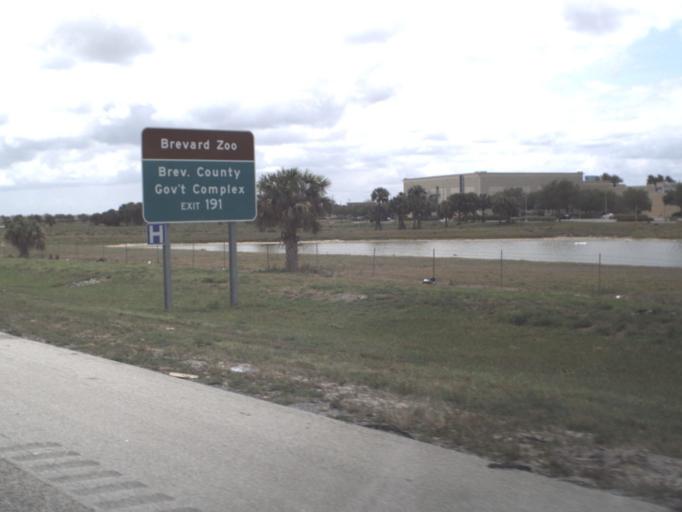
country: US
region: Florida
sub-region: Brevard County
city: Rockledge
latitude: 28.2450
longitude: -80.7229
